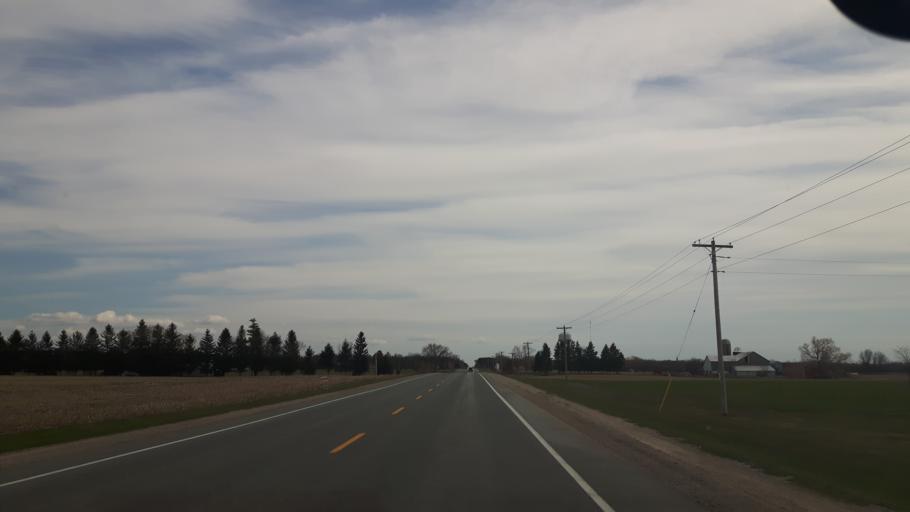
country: CA
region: Ontario
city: Goderich
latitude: 43.6963
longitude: -81.7057
